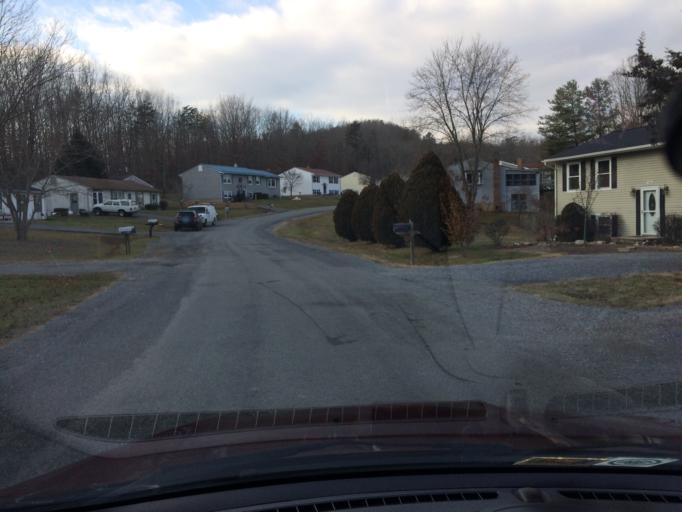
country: US
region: Virginia
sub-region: Alleghany County
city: Clifton Forge
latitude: 37.8337
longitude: -79.7916
